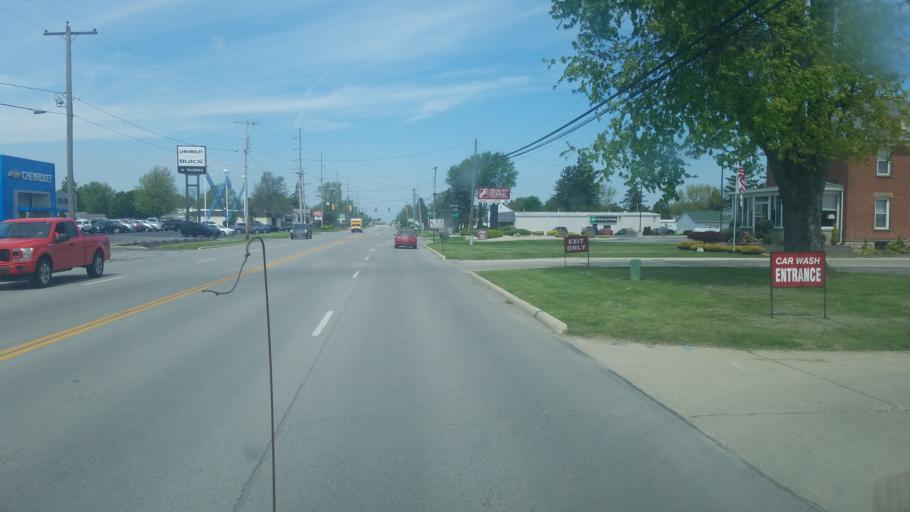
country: US
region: Ohio
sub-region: Sandusky County
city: Stony Prairie
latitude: 41.3603
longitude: -83.1446
